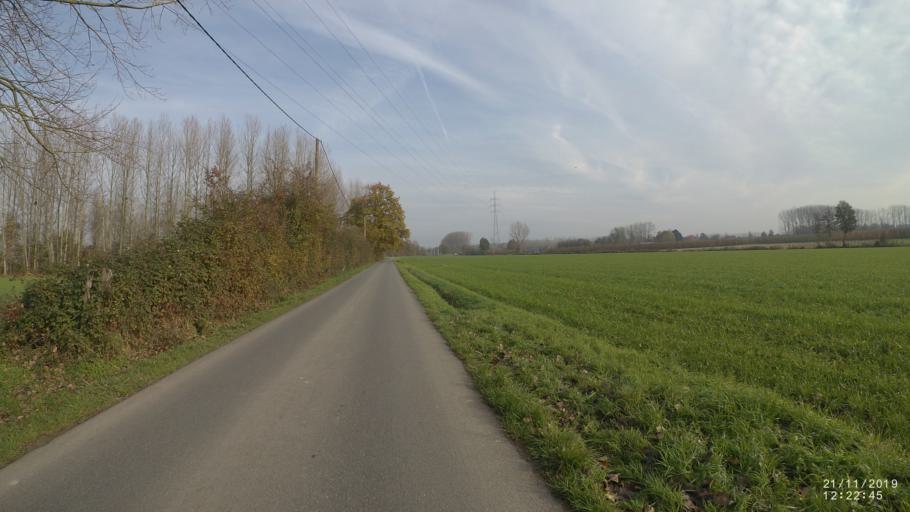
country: BE
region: Flanders
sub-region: Provincie Limburg
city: Alken
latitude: 50.8616
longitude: 5.2631
